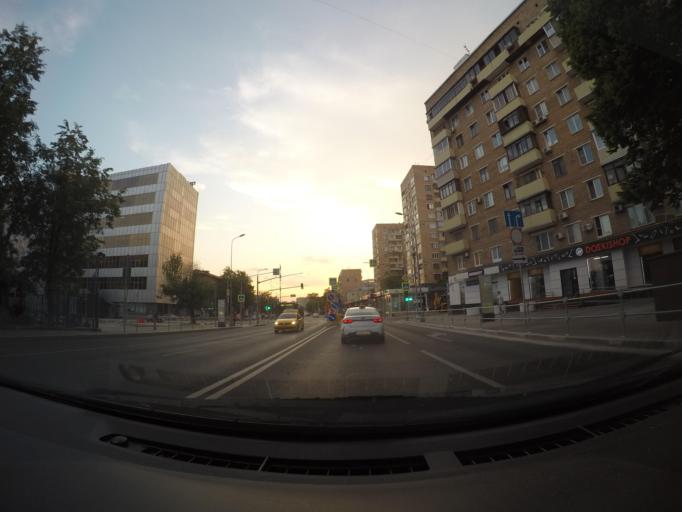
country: RU
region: Moscow
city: Lefortovo
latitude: 55.7820
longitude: 37.7102
